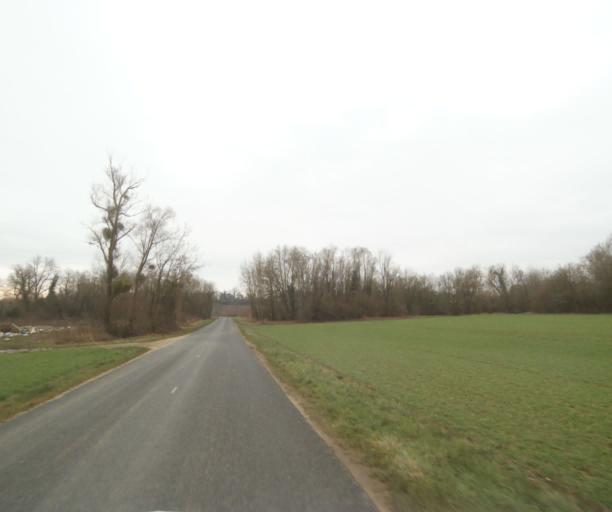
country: FR
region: Champagne-Ardenne
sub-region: Departement de la Haute-Marne
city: Villiers-en-Lieu
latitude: 48.6410
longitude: 4.8384
